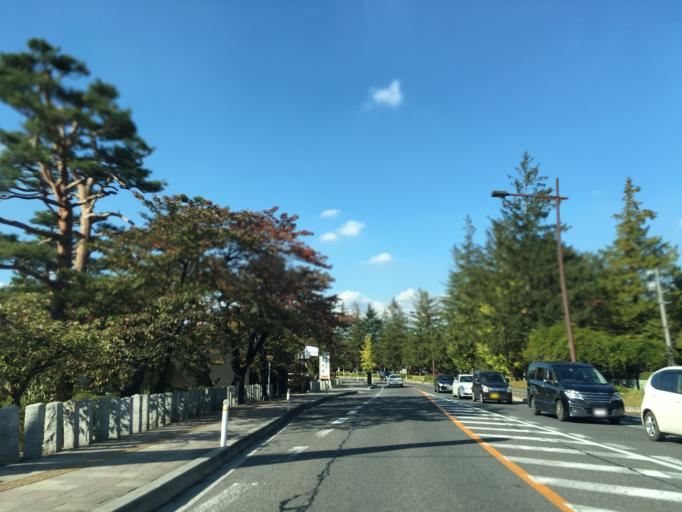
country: JP
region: Fukushima
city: Koriyama
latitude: 37.3961
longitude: 140.3546
